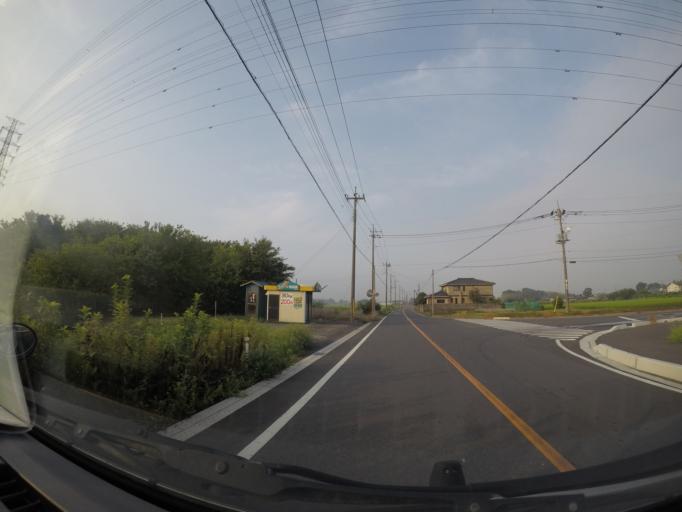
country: JP
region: Tochigi
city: Fujioka
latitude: 36.2745
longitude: 139.6786
